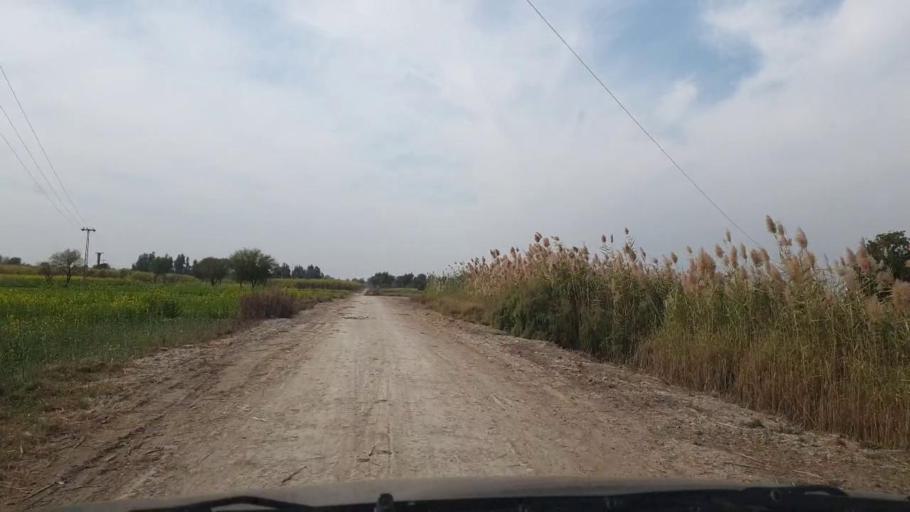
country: PK
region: Sindh
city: Sinjhoro
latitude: 26.0875
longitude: 68.8278
